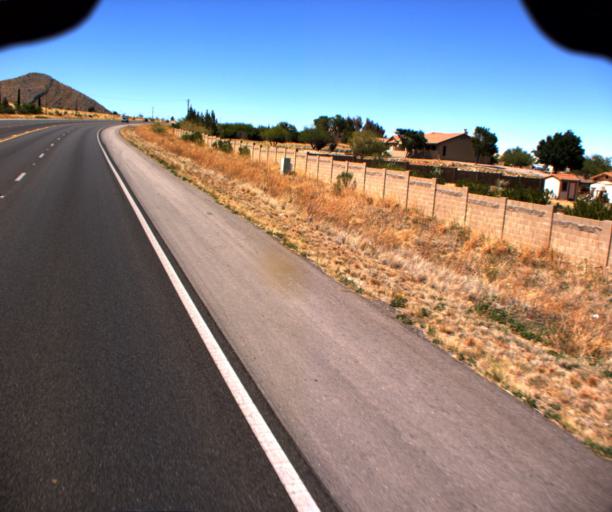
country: US
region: Arizona
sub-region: Cochise County
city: Sierra Vista Southeast
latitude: 31.4434
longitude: -110.2543
